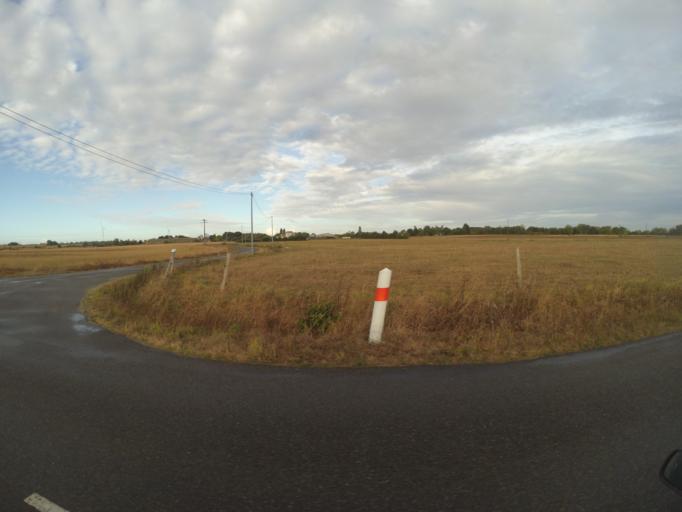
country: FR
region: Pays de la Loire
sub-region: Departement de la Loire-Atlantique
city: La Planche
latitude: 47.0119
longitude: -1.4558
